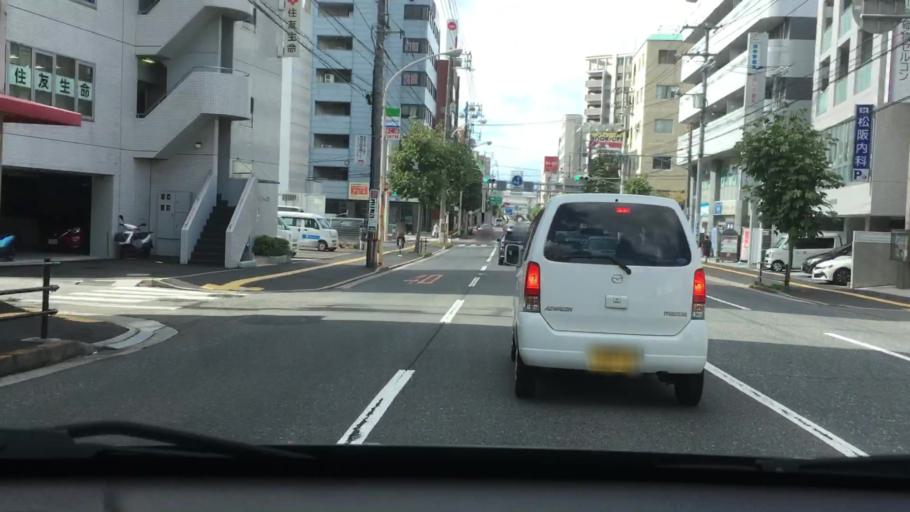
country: JP
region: Hiroshima
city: Hiroshima-shi
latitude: 34.3953
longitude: 132.4267
